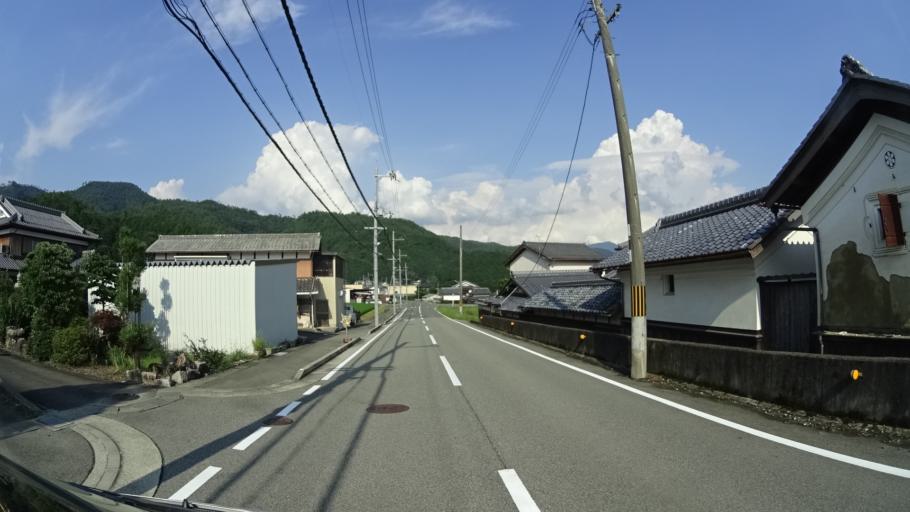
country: JP
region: Kyoto
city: Kameoka
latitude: 35.1000
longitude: 135.5354
